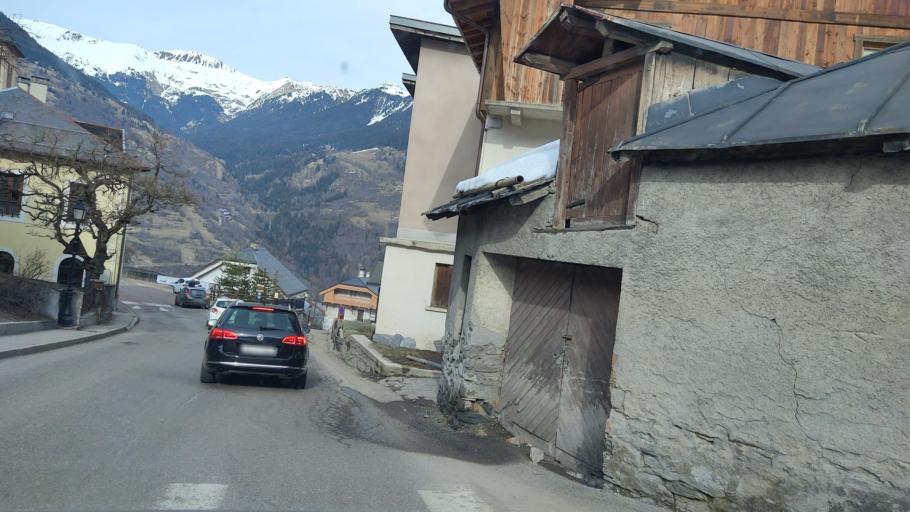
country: FR
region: Rhone-Alpes
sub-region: Departement de la Savoie
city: Saint-Bon-Tarentaise
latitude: 45.4338
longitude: 6.6371
